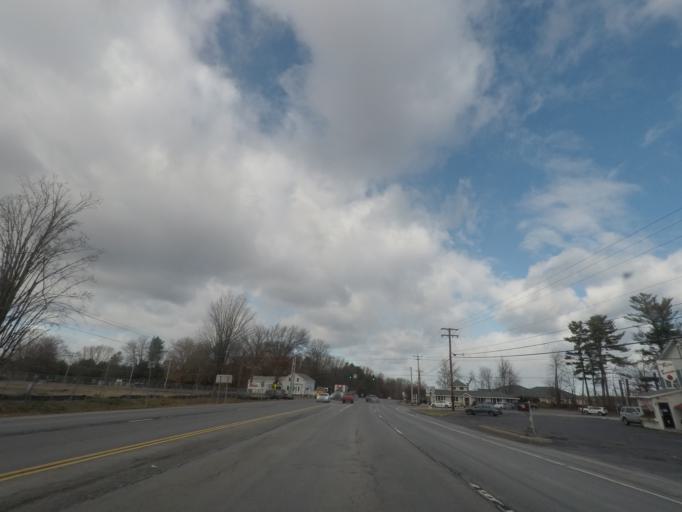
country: US
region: New York
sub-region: Saratoga County
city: Ballston Spa
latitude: 42.9935
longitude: -73.7904
